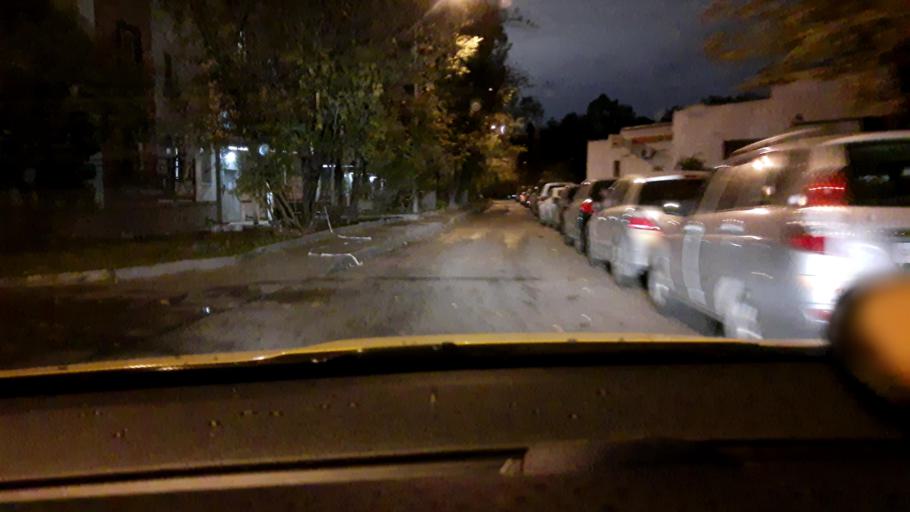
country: RU
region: Moscow
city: Novokuz'minki
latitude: 55.7115
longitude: 37.7882
